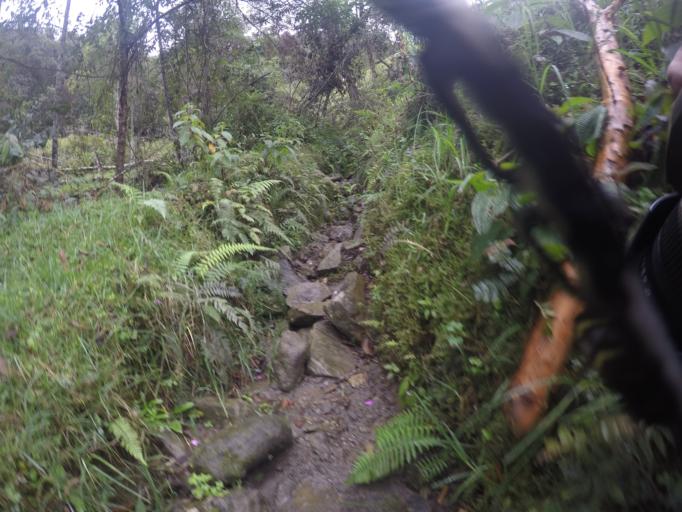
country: CO
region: Tolima
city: Cajamarca
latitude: 4.5293
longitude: -75.3544
